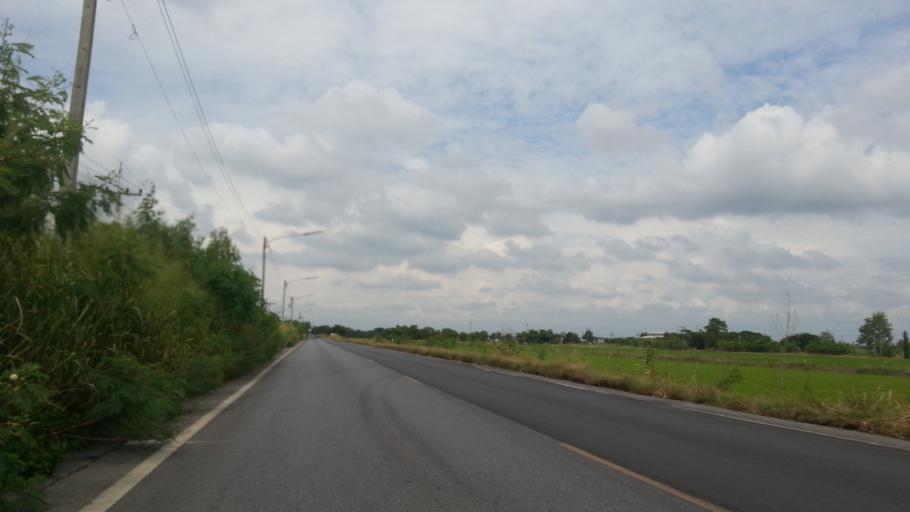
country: TH
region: Pathum Thani
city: Nong Suea
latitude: 14.0481
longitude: 100.8447
